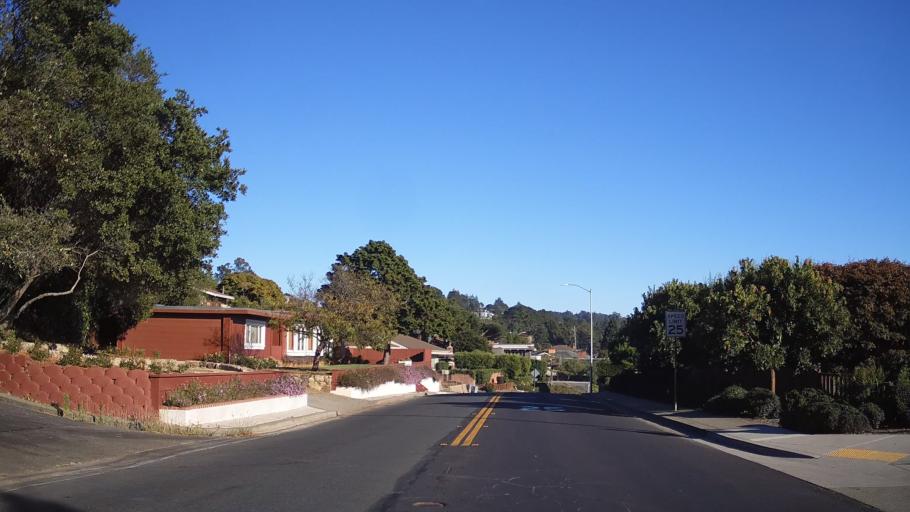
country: US
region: California
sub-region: Contra Costa County
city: Kensington
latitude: 37.9170
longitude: -122.2842
